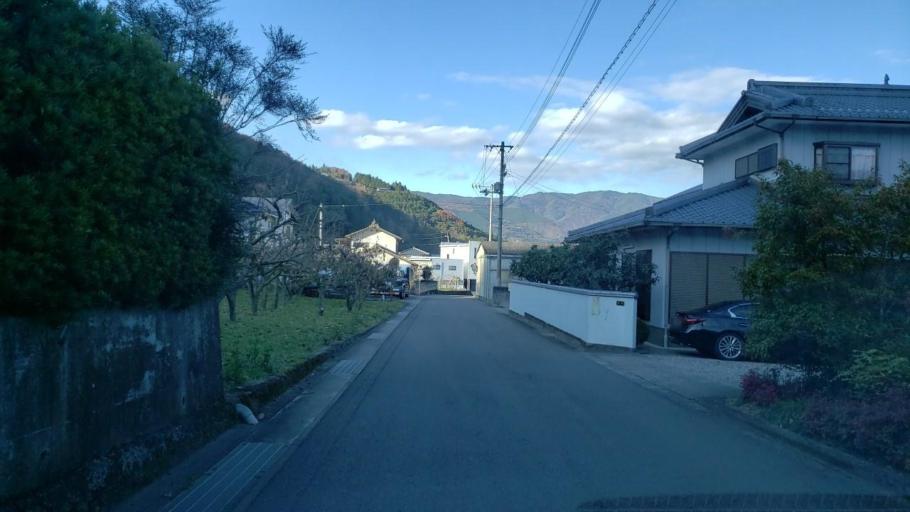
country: JP
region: Tokushima
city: Wakimachi
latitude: 34.0246
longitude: 134.0298
